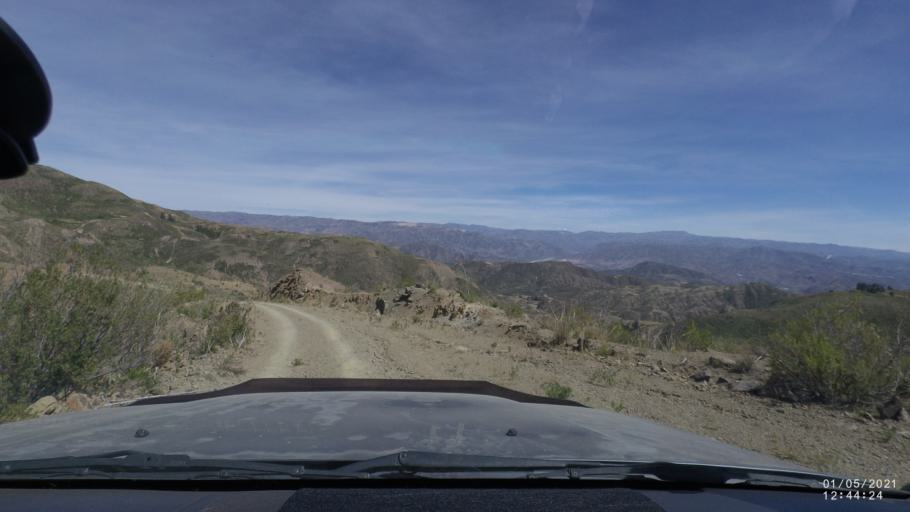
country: BO
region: Cochabamba
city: Capinota
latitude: -17.6823
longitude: -66.1601
